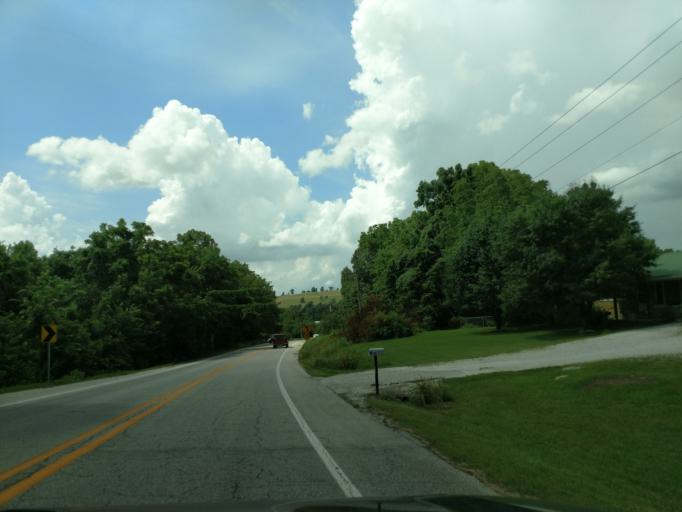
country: US
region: Arkansas
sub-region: Boone County
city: Harrison
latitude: 36.2901
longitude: -93.2389
